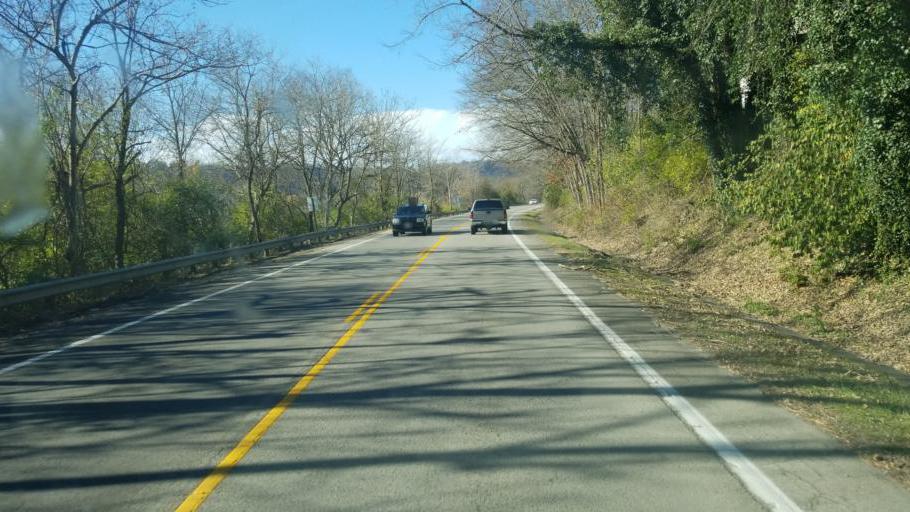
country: US
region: Ohio
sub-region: Brown County
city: Aberdeen
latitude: 38.6518
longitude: -83.7530
